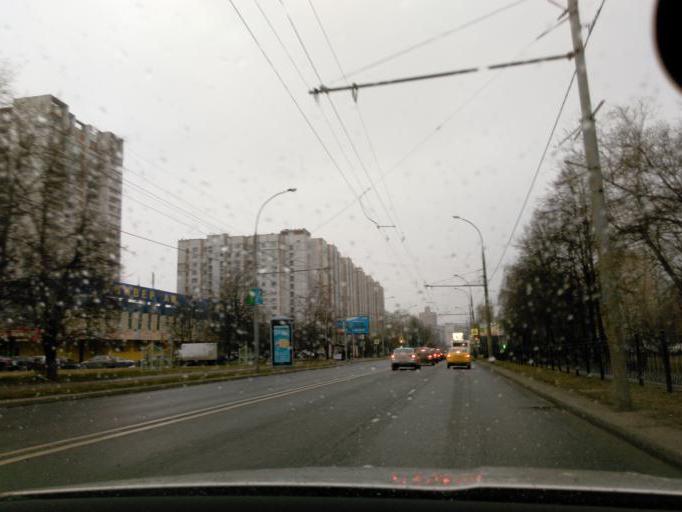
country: RU
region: Moskovskaya
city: Levoberezhnyy
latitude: 55.8487
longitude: 37.4531
